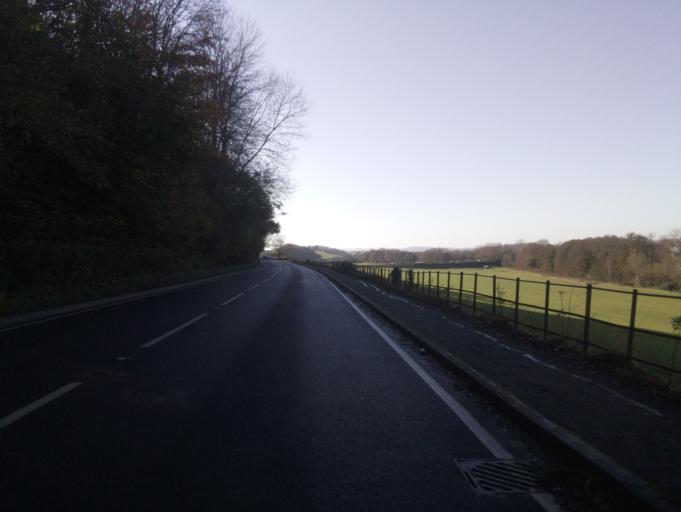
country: GB
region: England
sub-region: Dorset
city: Sherborne
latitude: 50.9418
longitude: -2.5145
